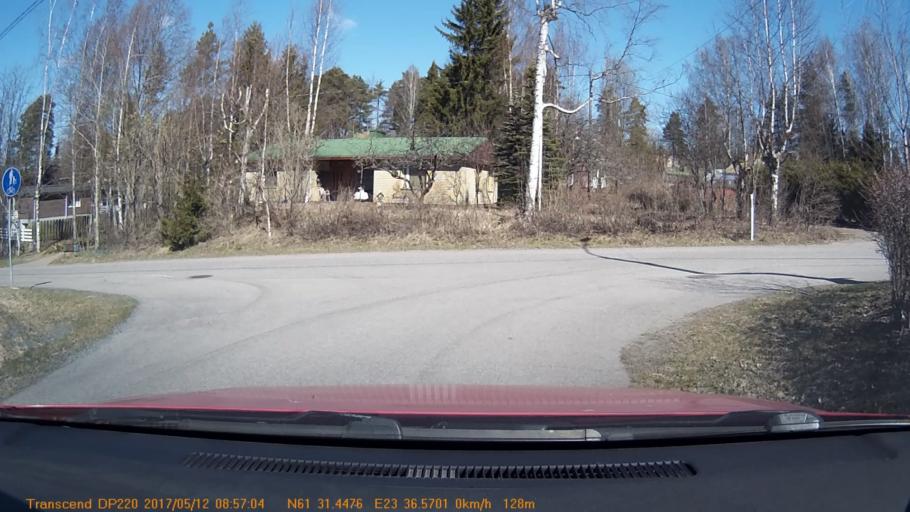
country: FI
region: Pirkanmaa
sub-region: Tampere
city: Yloejaervi
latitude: 61.5241
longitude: 23.6095
